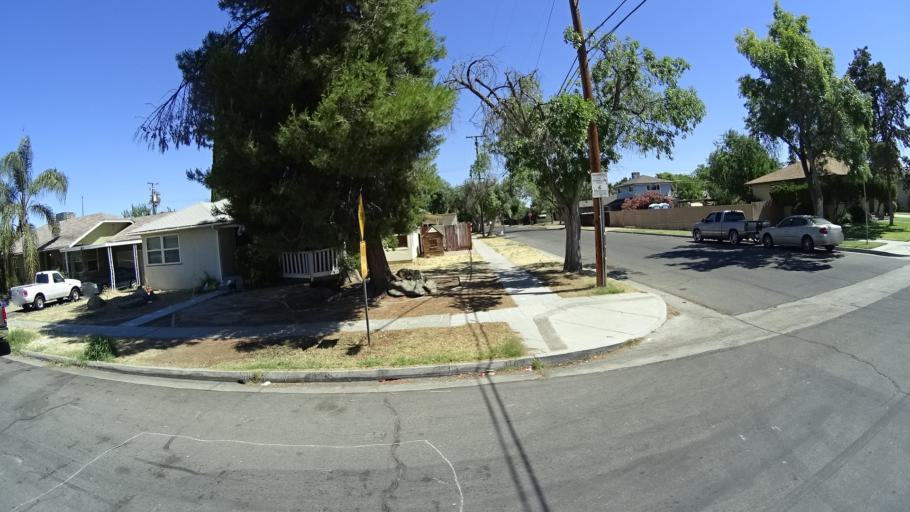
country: US
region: California
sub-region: Fresno County
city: Fresno
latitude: 36.7884
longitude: -119.8244
